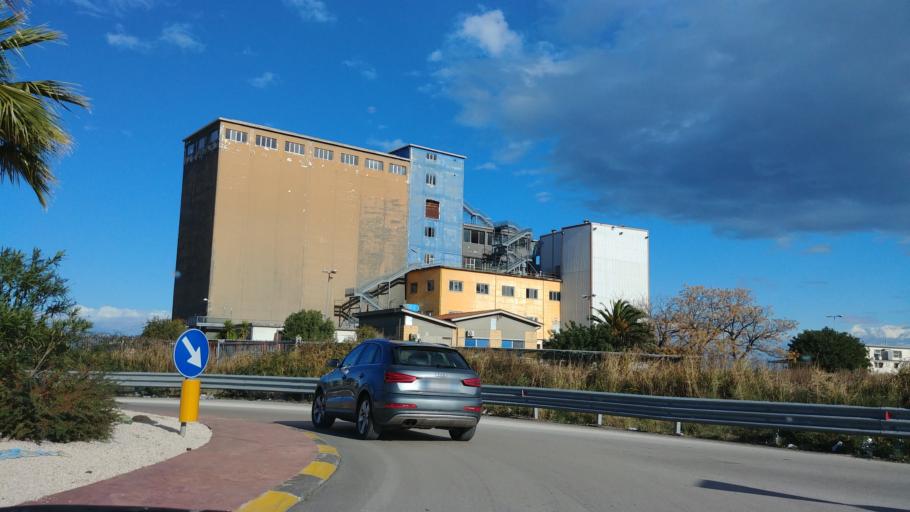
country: IT
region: Molise
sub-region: Provincia di Campobasso
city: Termoli
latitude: 41.9803
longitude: 15.0074
